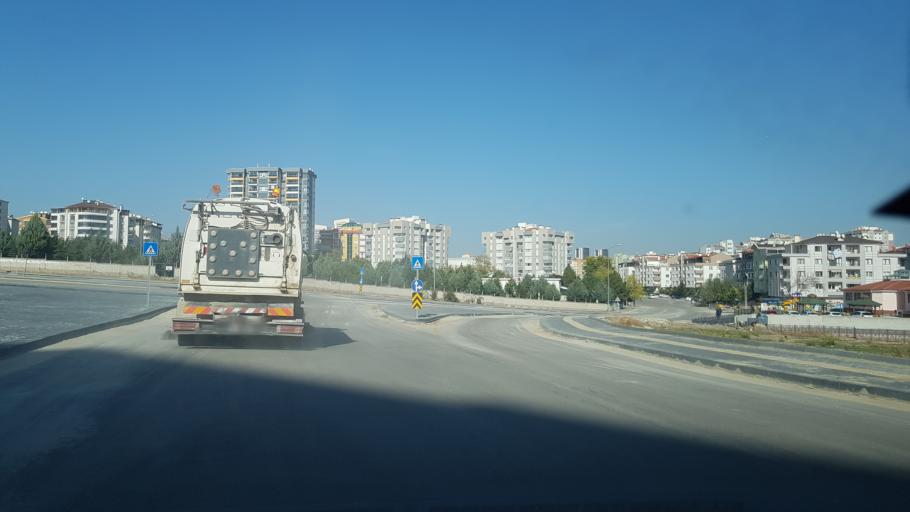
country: TR
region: Ankara
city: Etimesgut
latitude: 39.9726
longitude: 32.6122
